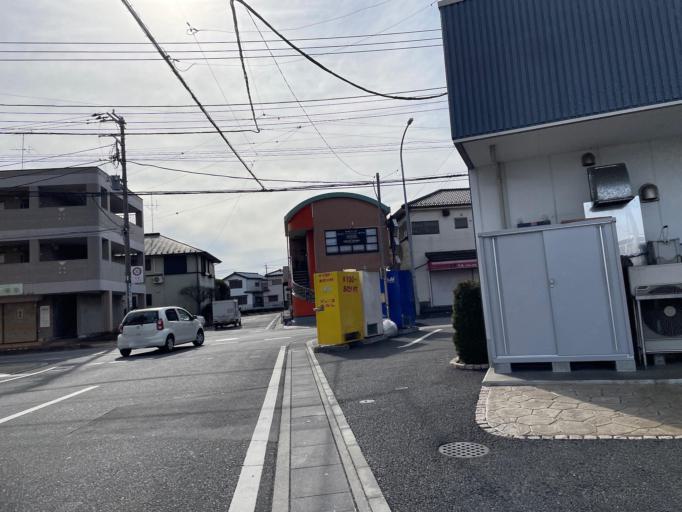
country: JP
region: Saitama
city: Sayama
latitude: 35.8222
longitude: 139.4089
